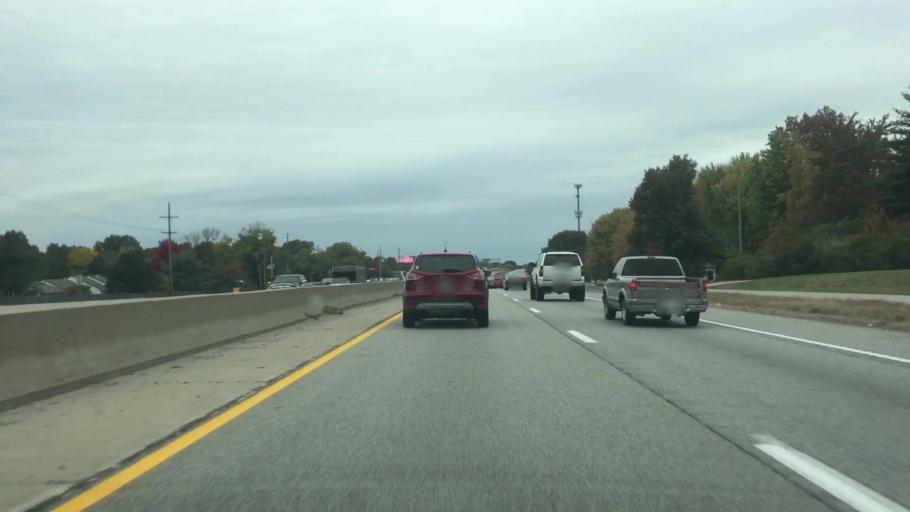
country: US
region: Missouri
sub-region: Jackson County
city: Lees Summit
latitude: 38.9071
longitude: -94.3865
